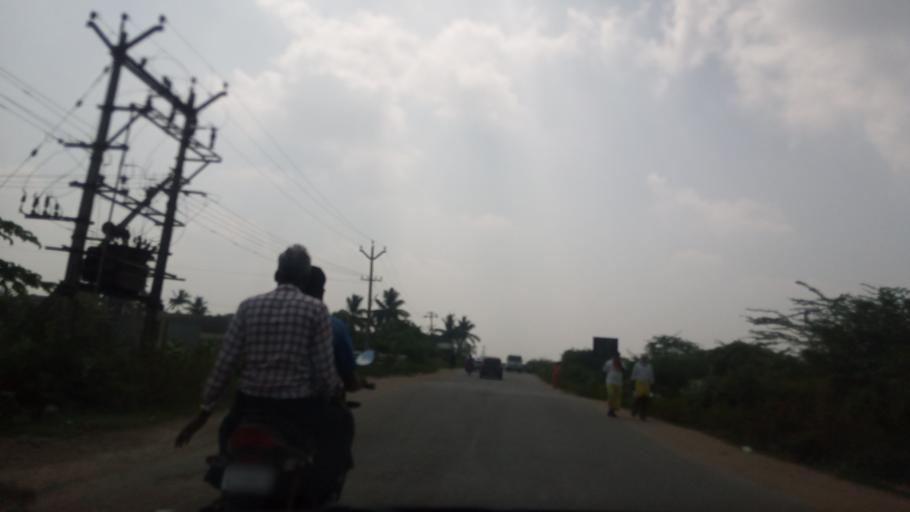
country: IN
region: Tamil Nadu
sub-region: Vellore
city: Arakkonam
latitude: 13.0556
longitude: 79.6741
